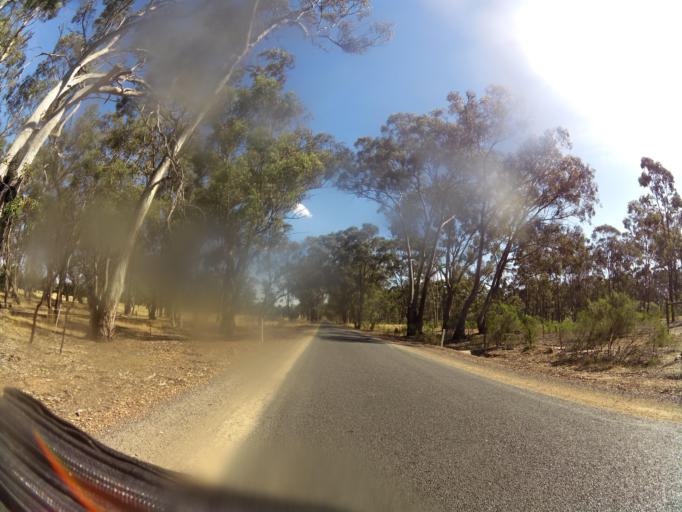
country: AU
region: Victoria
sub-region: Campaspe
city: Kyabram
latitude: -36.8687
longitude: 145.0868
